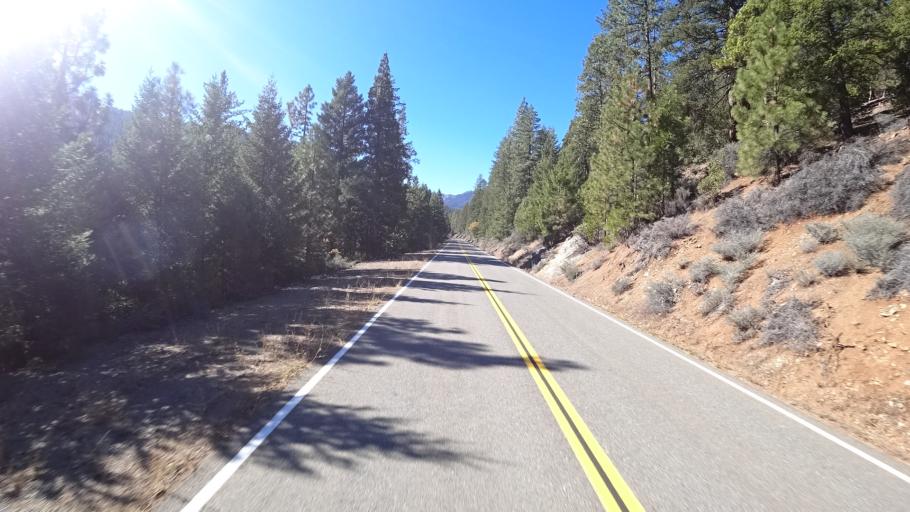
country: US
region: California
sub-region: Siskiyou County
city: Weed
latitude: 41.2802
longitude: -122.8556
